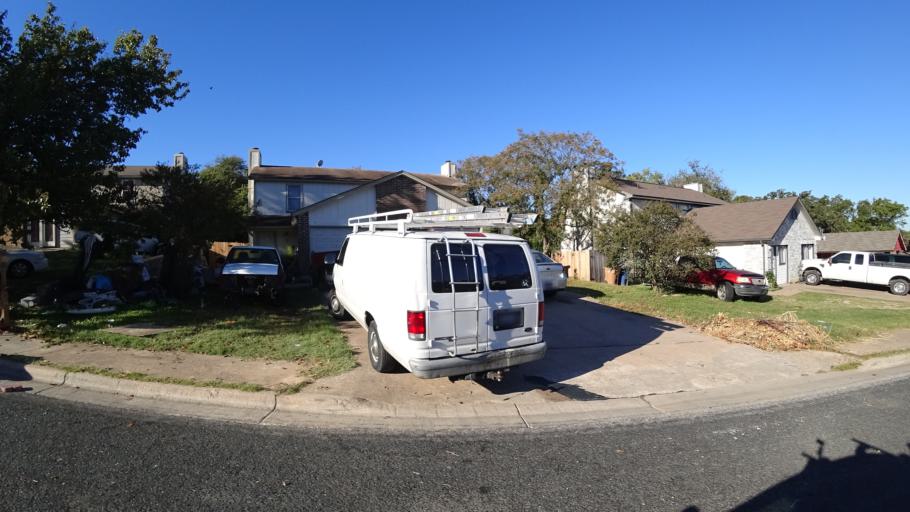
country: US
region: Texas
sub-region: Travis County
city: Hornsby Bend
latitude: 30.2238
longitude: -97.6664
